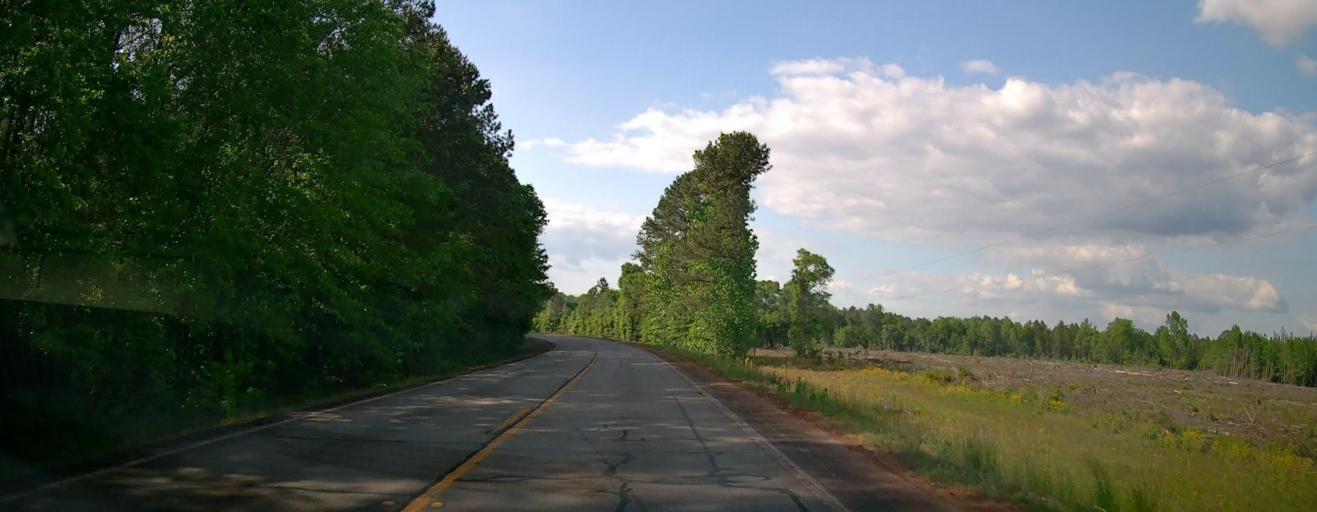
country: US
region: Georgia
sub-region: Washington County
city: Tennille
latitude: 32.9039
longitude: -82.9706
